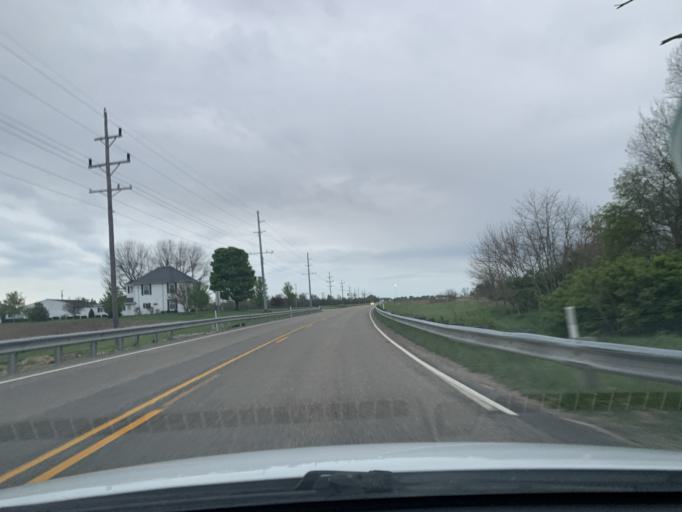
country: US
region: Indiana
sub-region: Cass County
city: Logansport
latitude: 40.8874
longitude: -86.2890
